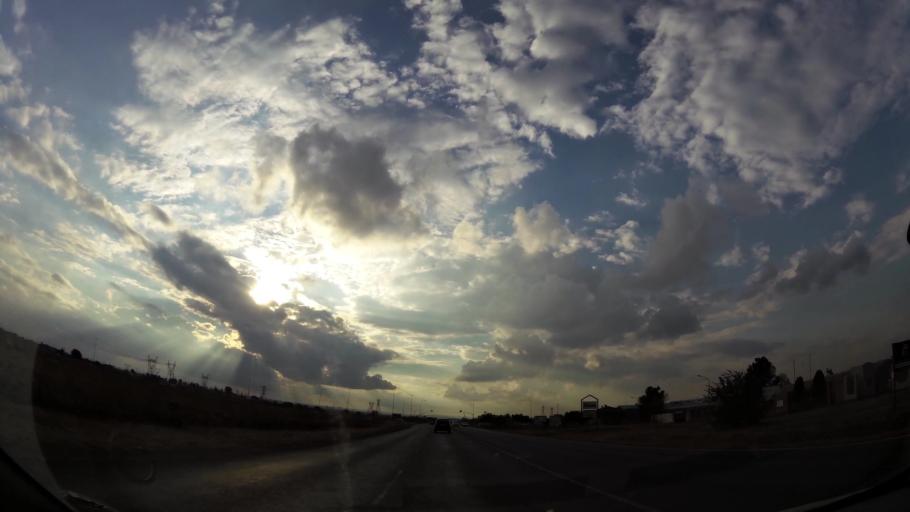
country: ZA
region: Gauteng
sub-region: Sedibeng District Municipality
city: Vanderbijlpark
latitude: -26.6794
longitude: 27.7950
